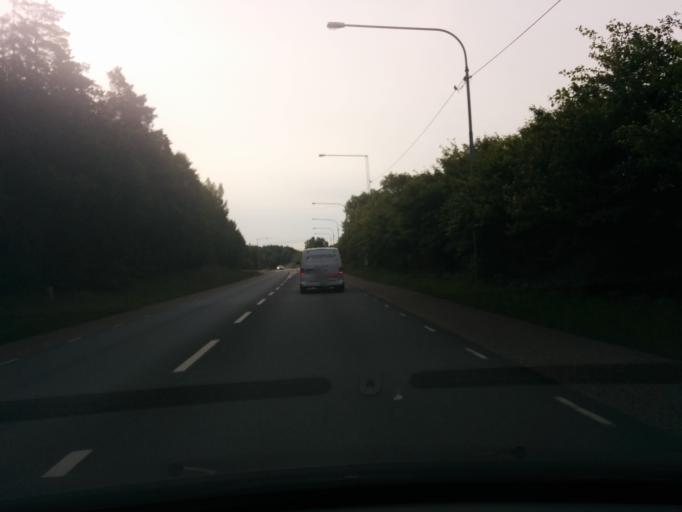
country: SE
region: Stockholm
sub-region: Norrtalje Kommun
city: Bergshamra
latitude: 59.4155
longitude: 18.0161
